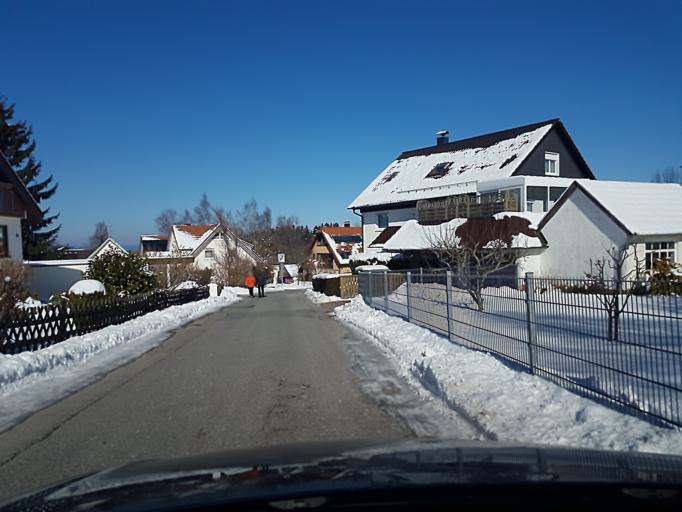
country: DE
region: Baden-Wuerttemberg
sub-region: Freiburg Region
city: Hardt
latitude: 48.1855
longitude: 8.4043
